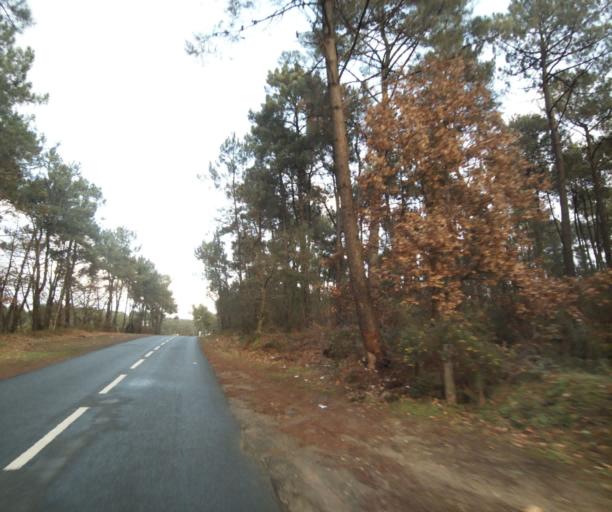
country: FR
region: Pays de la Loire
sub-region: Departement de la Sarthe
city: Ruaudin
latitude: 47.9643
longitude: 0.2284
